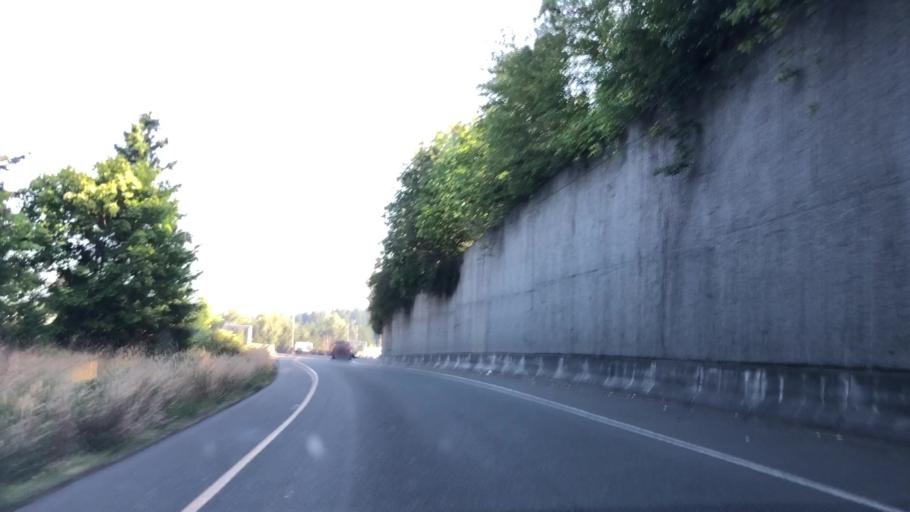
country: US
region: Washington
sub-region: Snohomish County
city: Mountlake Terrace
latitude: 47.7828
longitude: -122.3176
